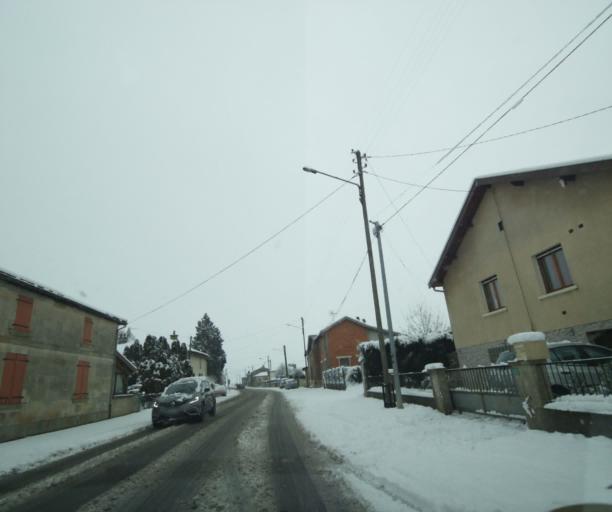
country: FR
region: Champagne-Ardenne
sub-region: Departement de la Haute-Marne
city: Saint-Dizier
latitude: 48.5837
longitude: 4.9031
